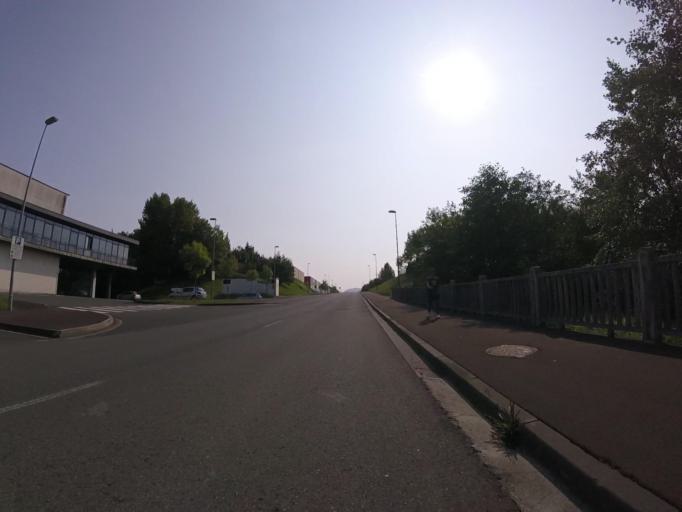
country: ES
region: Basque Country
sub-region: Provincia de Guipuzcoa
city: Errenteria
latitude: 43.2990
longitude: -1.8958
